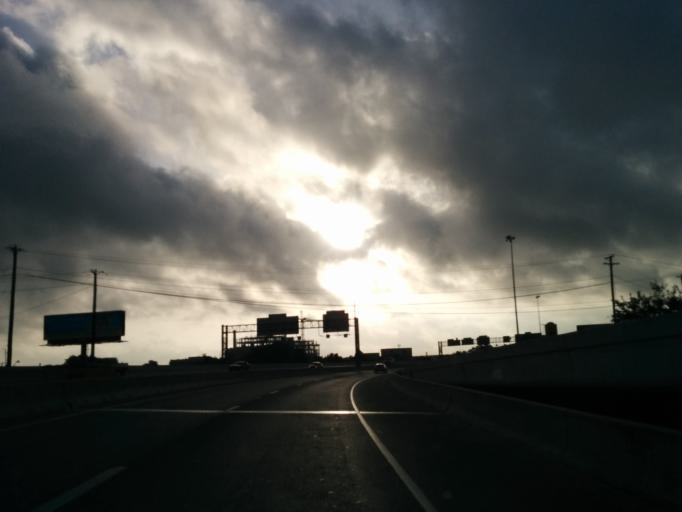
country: US
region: Texas
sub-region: Bexar County
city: San Antonio
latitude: 29.4401
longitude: -98.4863
